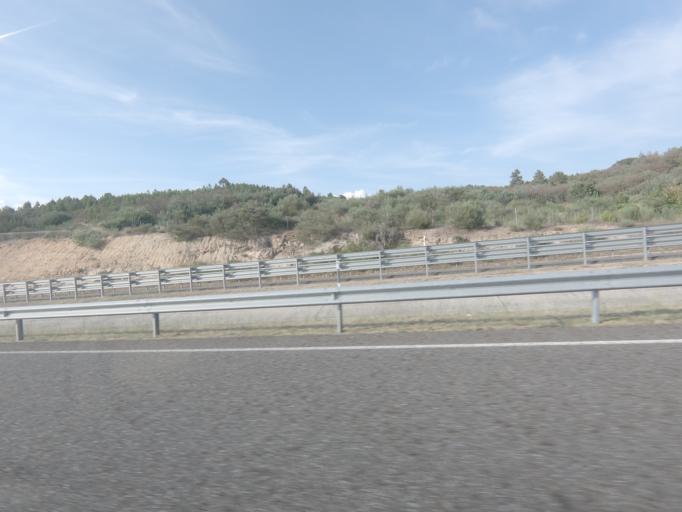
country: ES
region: Galicia
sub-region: Provincia de Ourense
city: Oimbra
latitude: 41.8554
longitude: -7.4223
